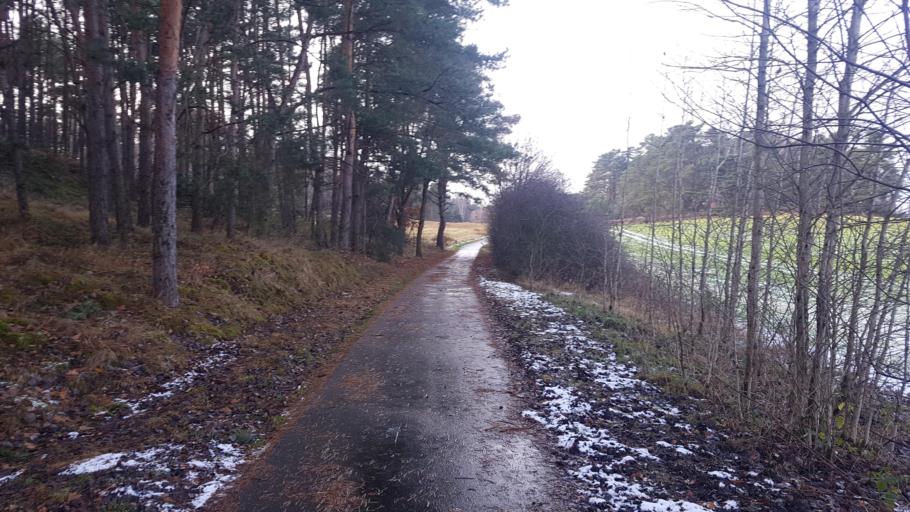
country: DE
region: Brandenburg
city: Hirschfeld
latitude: 51.3931
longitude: 13.5934
